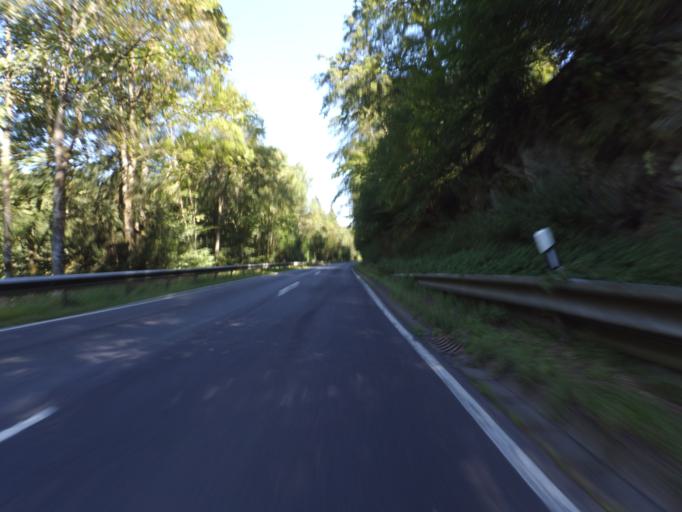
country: DE
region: Rheinland-Pfalz
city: Mullenbach
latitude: 50.1995
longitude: 7.0601
